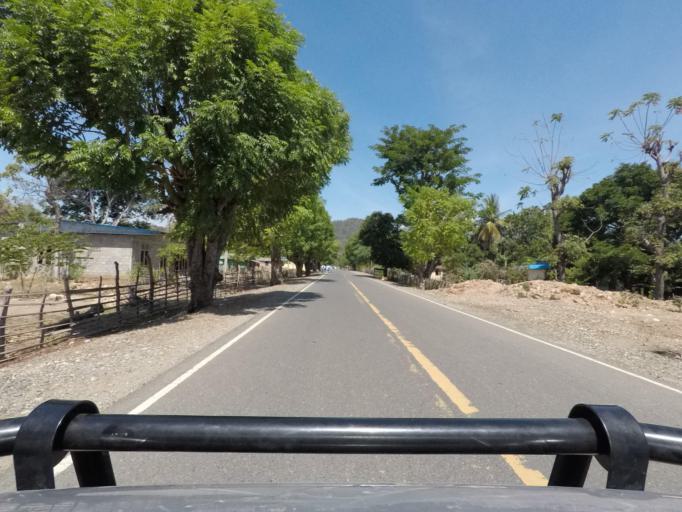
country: TL
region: Liquica
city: Maubara
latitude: -8.7903
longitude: 125.1015
